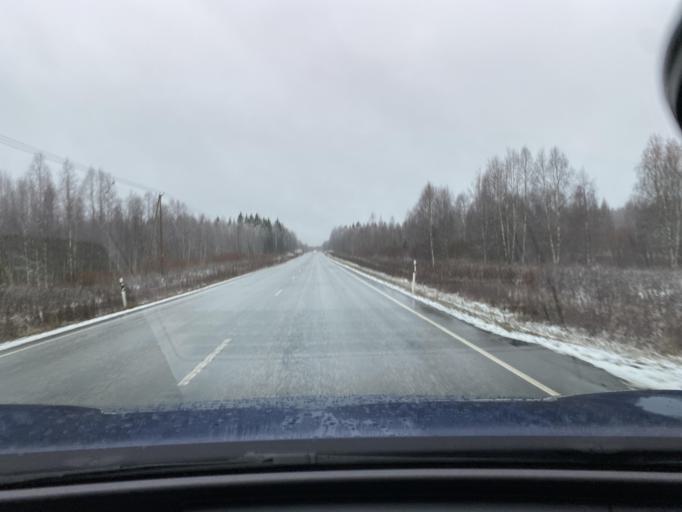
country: FI
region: Northern Ostrobothnia
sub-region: Oulu
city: Kiiminki
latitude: 65.1346
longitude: 25.8180
